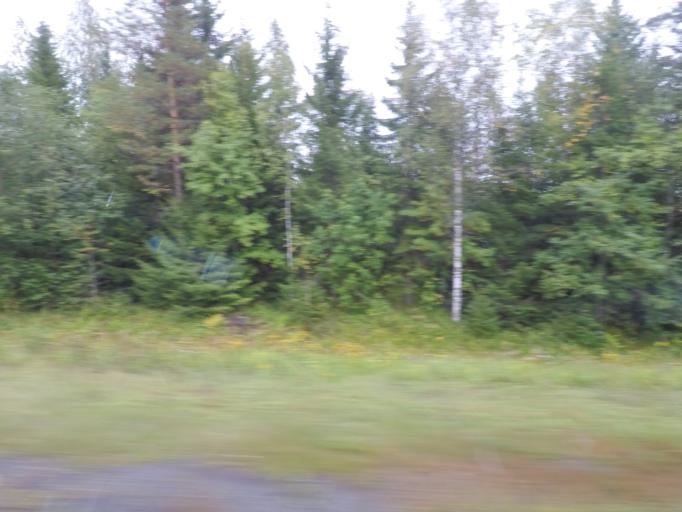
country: FI
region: Southern Savonia
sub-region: Pieksaemaeki
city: Juva
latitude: 62.0046
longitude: 27.8022
